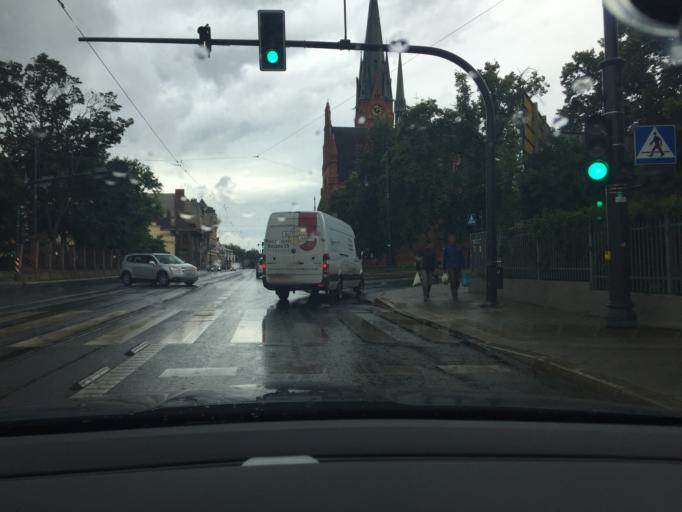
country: PL
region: Kujawsko-Pomorskie
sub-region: Torun
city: Torun
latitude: 53.0122
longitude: 18.6148
